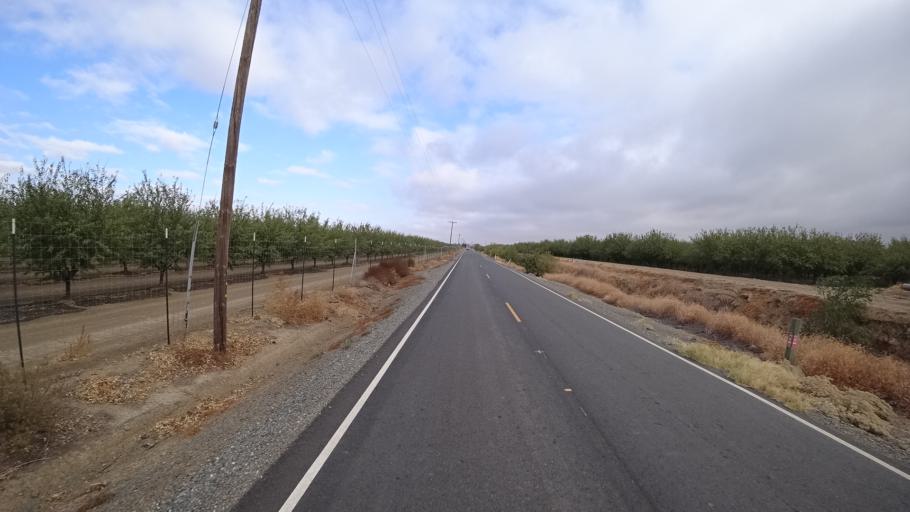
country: US
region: California
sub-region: Yolo County
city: Esparto
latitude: 38.7617
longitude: -122.0442
